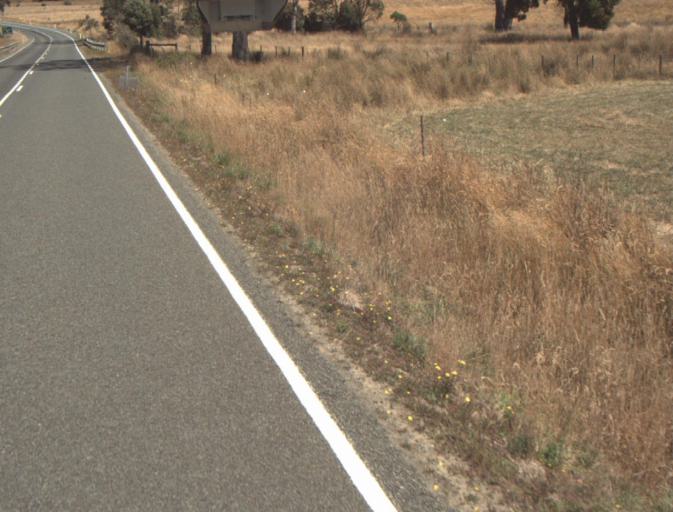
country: AU
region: Tasmania
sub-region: Launceston
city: Newstead
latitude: -41.3309
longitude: 147.3520
